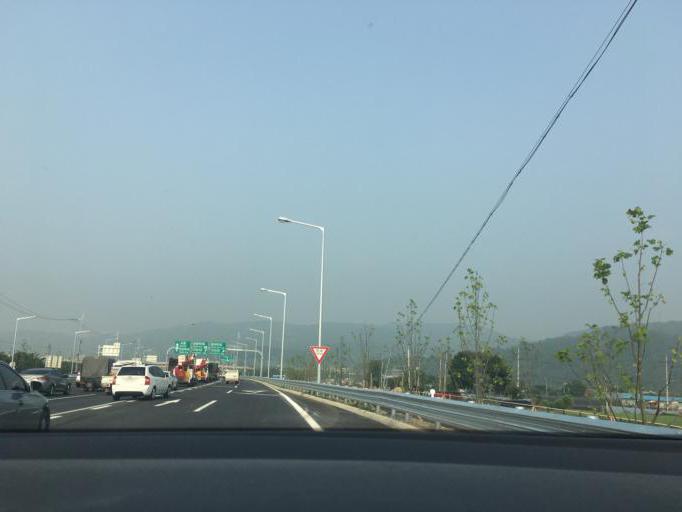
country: KR
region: Gyeonggi-do
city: Guri-si
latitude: 37.5763
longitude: 127.1362
